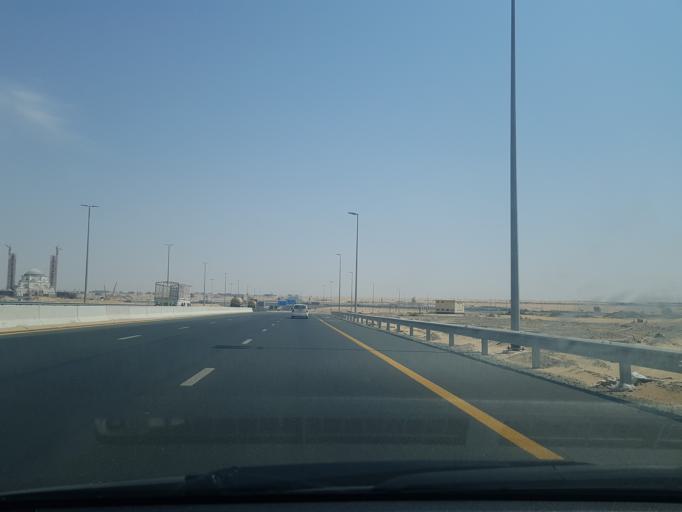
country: AE
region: Ash Shariqah
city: Sharjah
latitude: 25.2405
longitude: 55.5601
